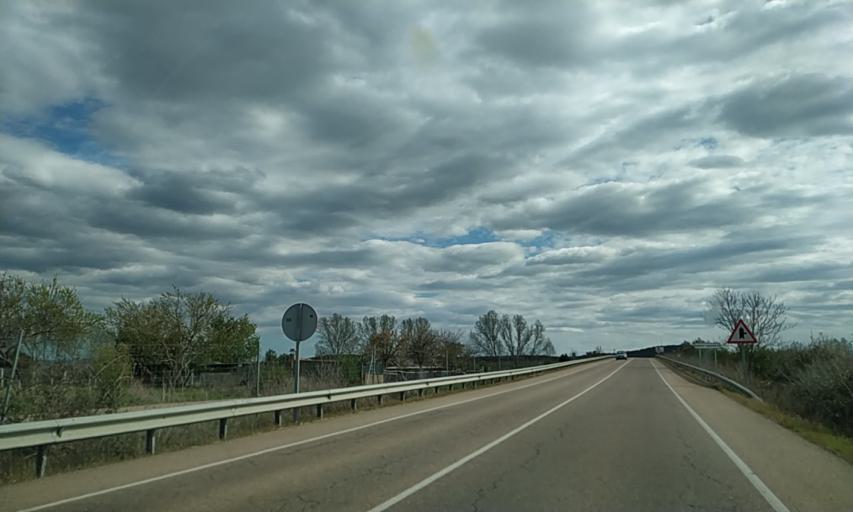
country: ES
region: Castille and Leon
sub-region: Provincia de Salamanca
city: Ciudad Rodrigo
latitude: 40.5873
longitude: -6.5373
